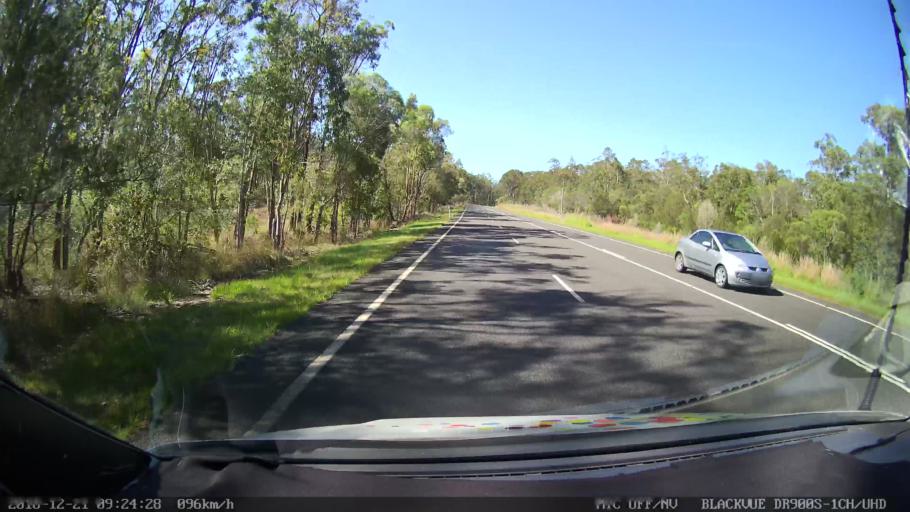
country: AU
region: New South Wales
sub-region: Clarence Valley
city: Maclean
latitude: -29.3678
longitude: 153.0161
